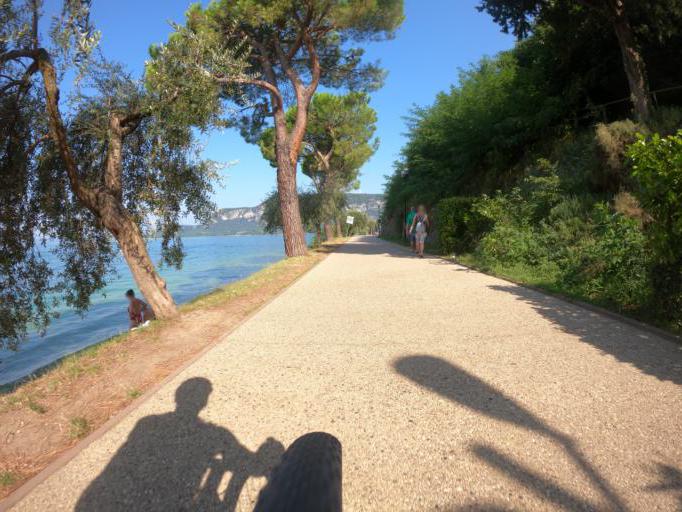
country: IT
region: Veneto
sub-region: Provincia di Verona
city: Garda
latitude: 45.5666
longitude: 10.7098
